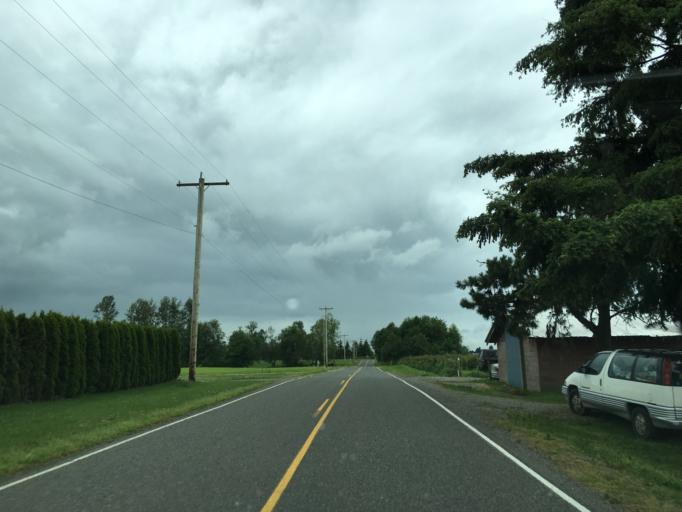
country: US
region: Washington
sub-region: Whatcom County
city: Everson
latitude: 48.9821
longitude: -122.3799
